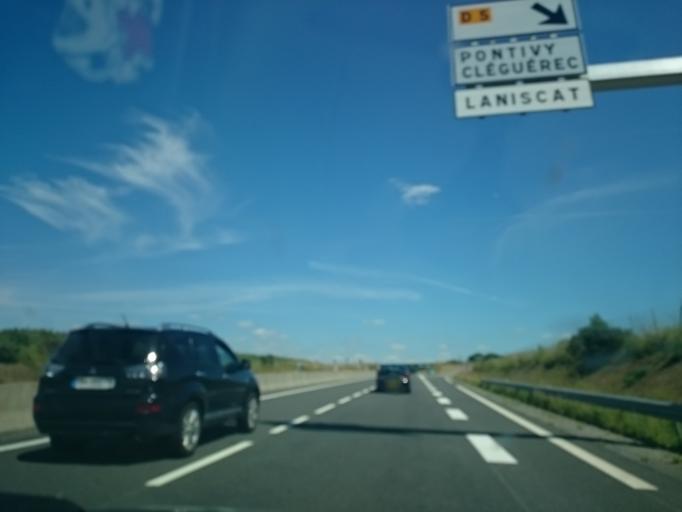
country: FR
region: Brittany
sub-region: Departement des Cotes-d'Armor
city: Gouarec
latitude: 48.2338
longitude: -3.1693
